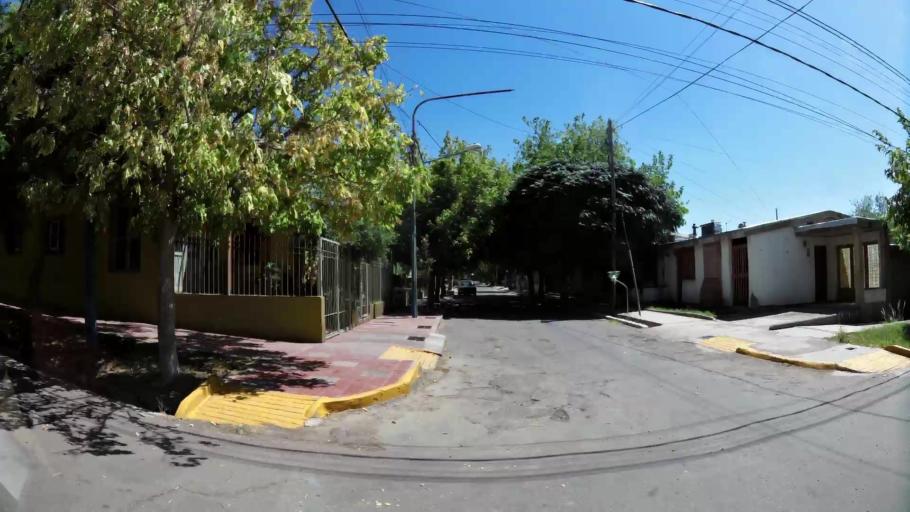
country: AR
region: Mendoza
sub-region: Departamento de Godoy Cruz
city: Godoy Cruz
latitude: -32.9376
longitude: -68.8748
